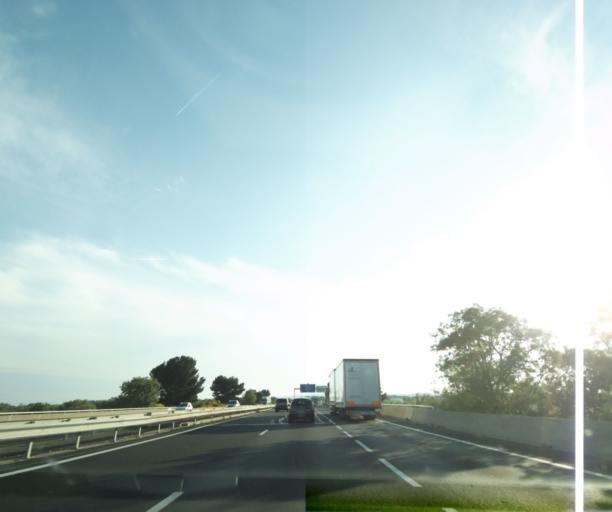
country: FR
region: Languedoc-Roussillon
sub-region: Departement de l'Aude
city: Narbonne
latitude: 43.1792
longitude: 3.0404
